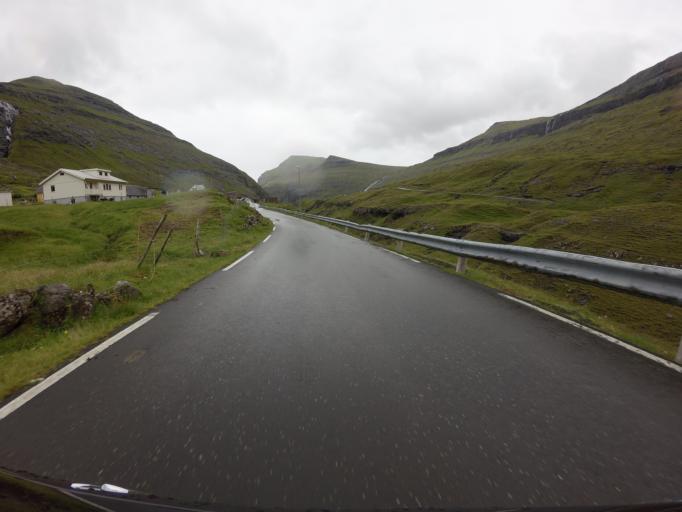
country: FO
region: Streymoy
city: Vestmanna
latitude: 62.2421
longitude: -7.1650
